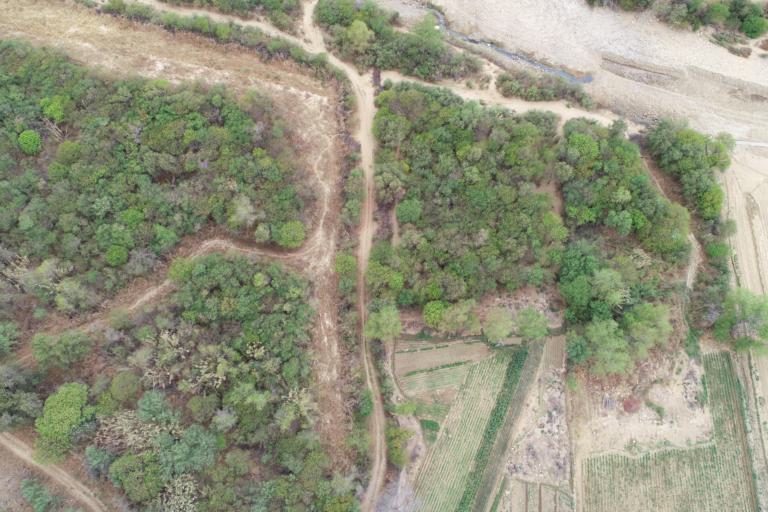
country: BO
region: Tarija
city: Tarija
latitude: -21.6003
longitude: -64.6158
